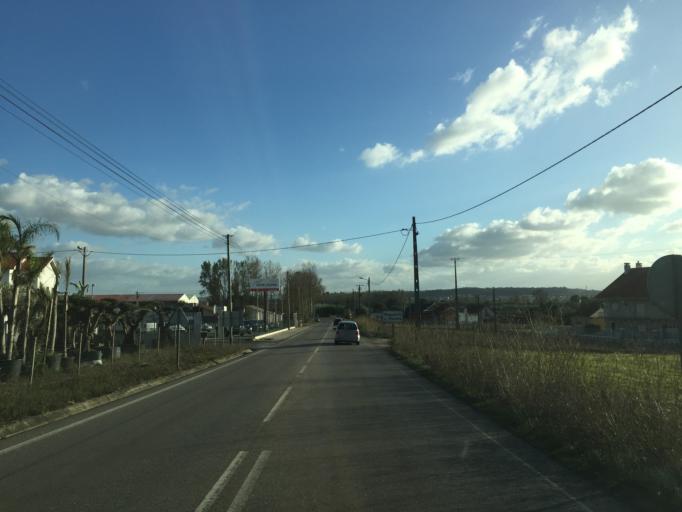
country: PT
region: Leiria
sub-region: Leiria
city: Amor
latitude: 39.8066
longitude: -8.8396
